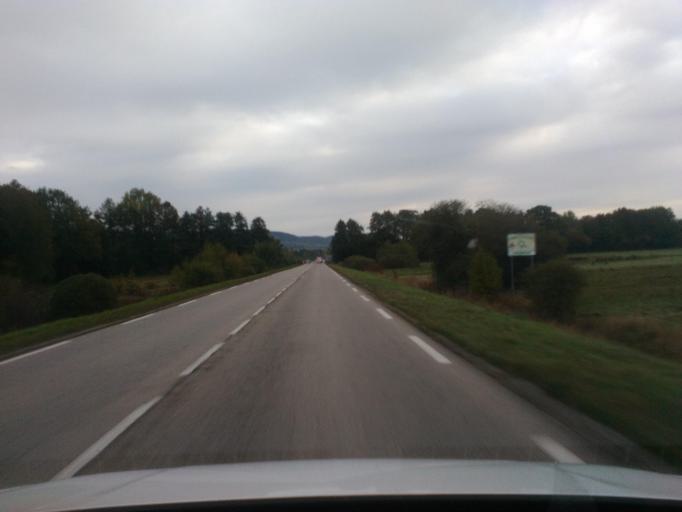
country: FR
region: Lorraine
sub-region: Departement des Vosges
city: Ban-de-Laveline
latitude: 48.2853
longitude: 7.0686
